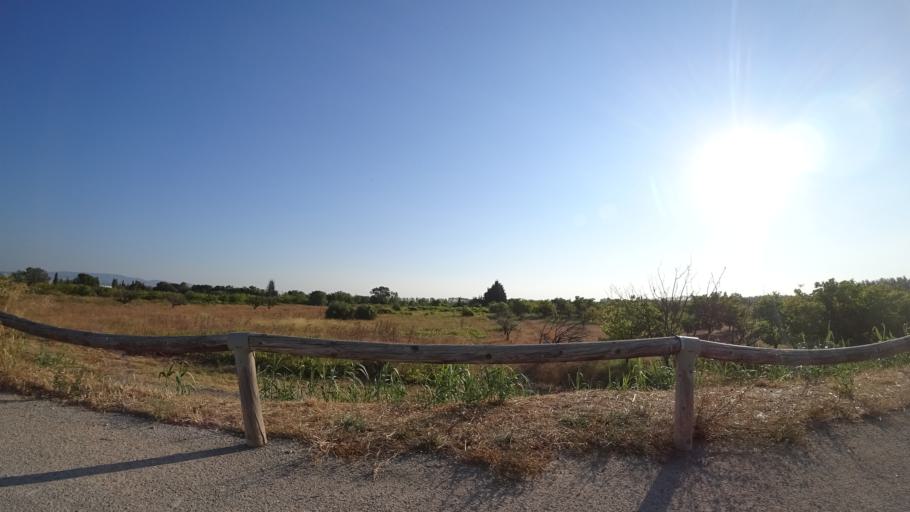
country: FR
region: Languedoc-Roussillon
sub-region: Departement des Pyrenees-Orientales
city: Pia
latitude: 42.7630
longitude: 2.9130
